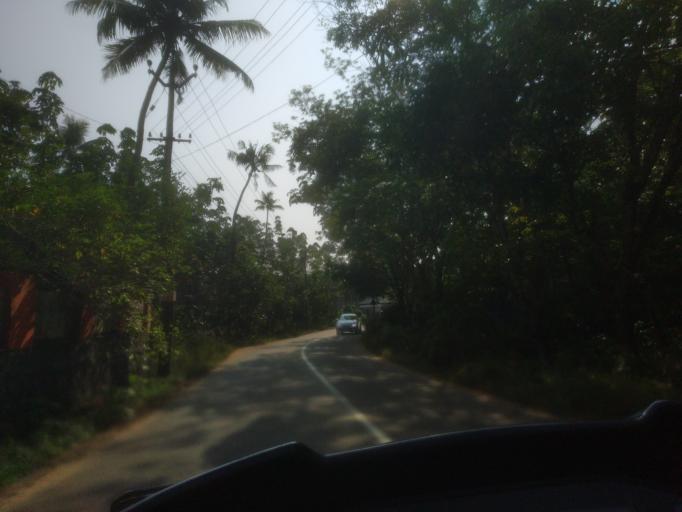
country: IN
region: Kerala
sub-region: Ernakulam
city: Piravam
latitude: 9.8643
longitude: 76.5336
